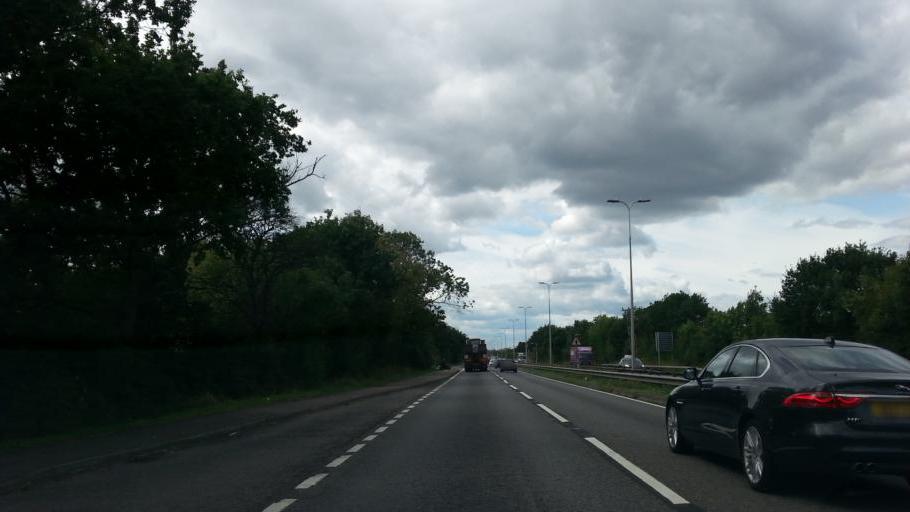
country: GB
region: England
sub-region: Essex
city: Brentwood
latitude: 51.5781
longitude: 0.3441
